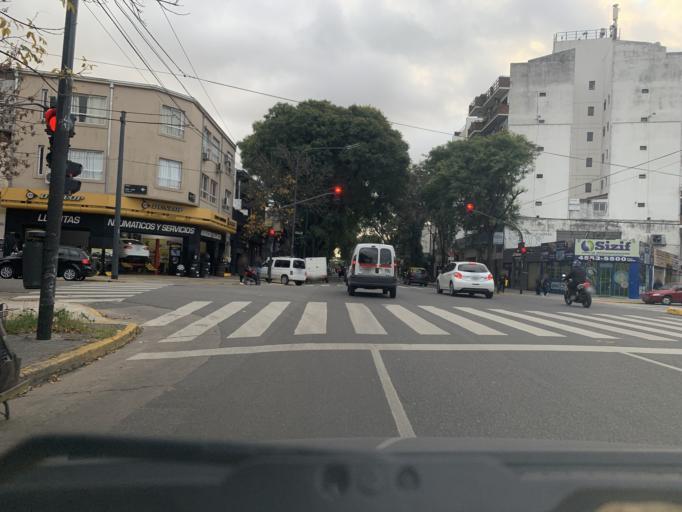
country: AR
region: Buenos Aires F.D.
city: Colegiales
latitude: -34.5791
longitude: -58.4671
